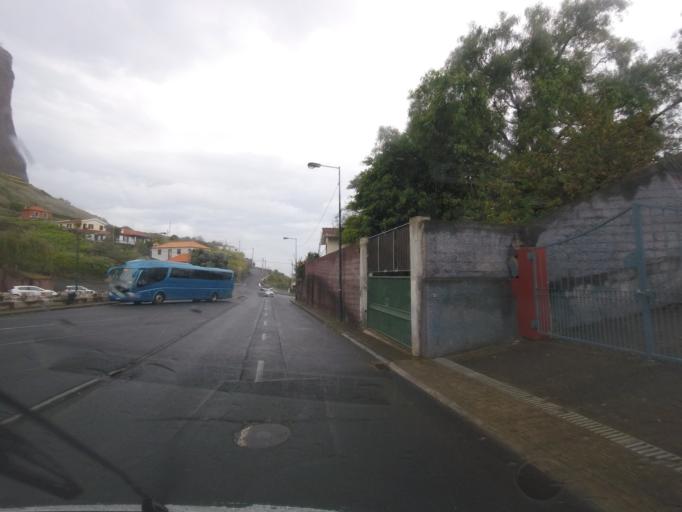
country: PT
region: Madeira
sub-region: Santana
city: Santana
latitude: 32.7722
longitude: -16.8298
